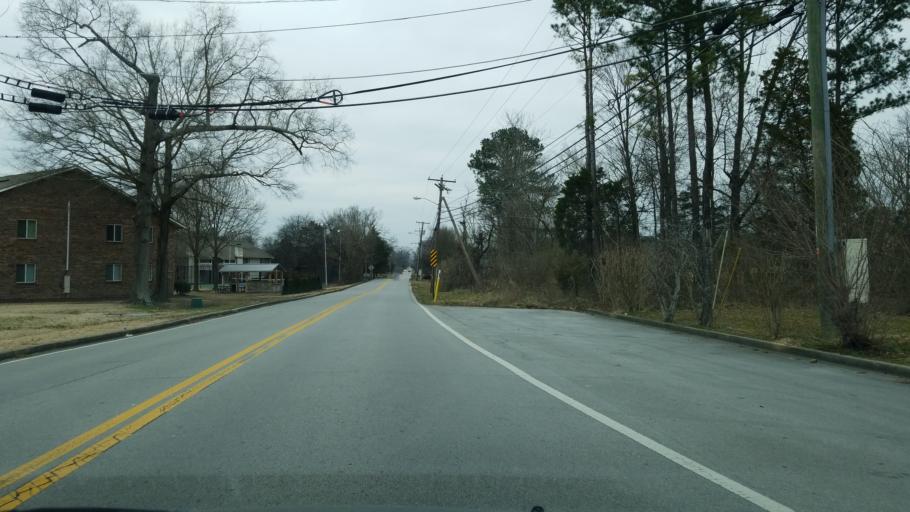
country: US
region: Tennessee
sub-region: Hamilton County
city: East Brainerd
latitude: 35.0525
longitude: -85.1507
